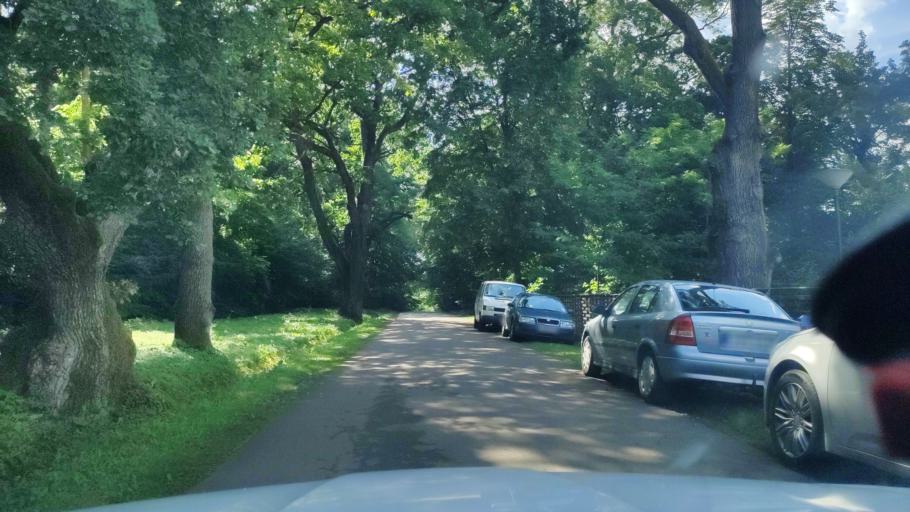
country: HU
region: Heves
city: Parad
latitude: 47.9232
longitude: 20.0569
